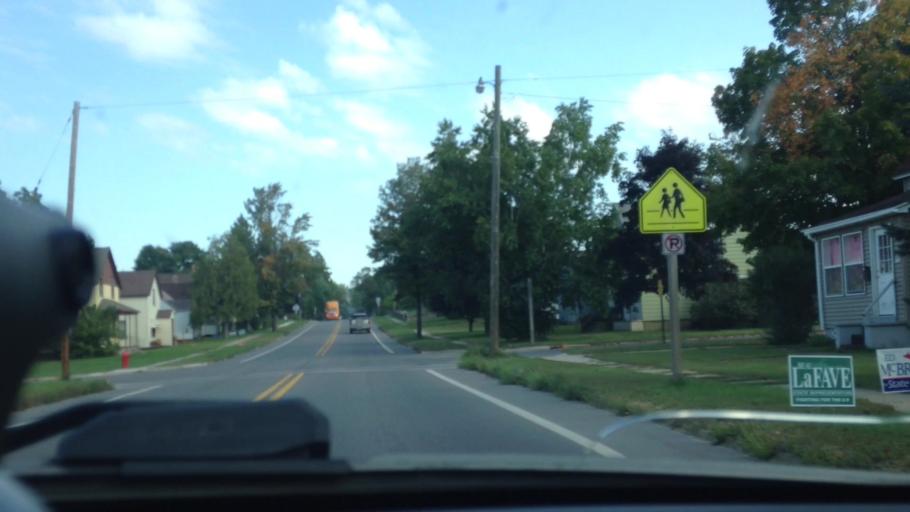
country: US
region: Michigan
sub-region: Dickinson County
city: Norway
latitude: 45.7821
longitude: -87.9098
